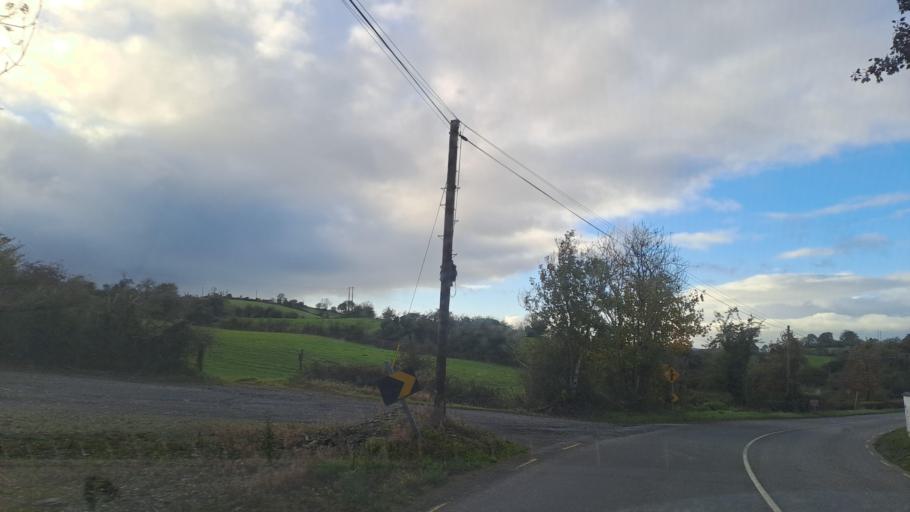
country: IE
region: Ulster
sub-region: County Monaghan
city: Castleblayney
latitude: 54.0400
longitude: -6.7905
